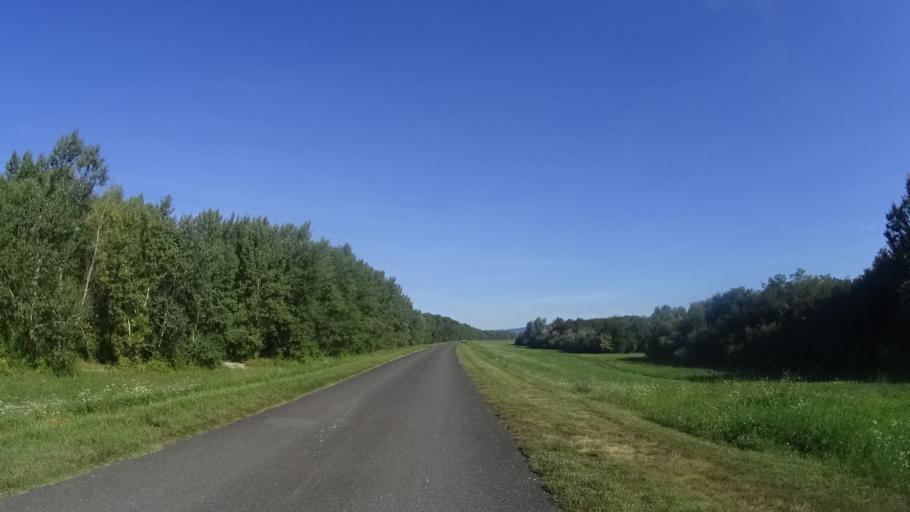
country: HU
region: Gyor-Moson-Sopron
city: Rajka
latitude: 48.0747
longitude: 17.1643
